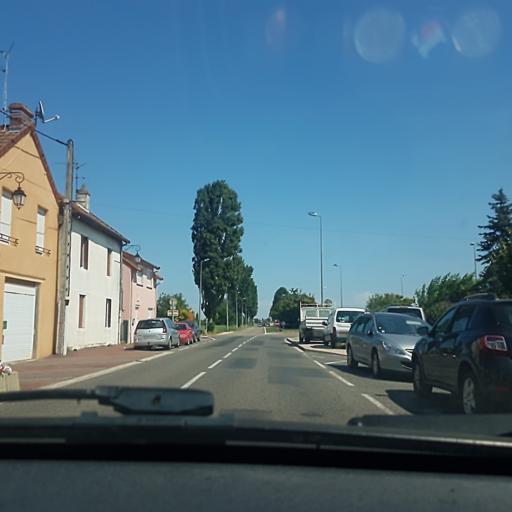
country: FR
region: Bourgogne
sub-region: Departement de Saone-et-Loire
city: Saint-Marcel
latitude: 46.7781
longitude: 4.8710
